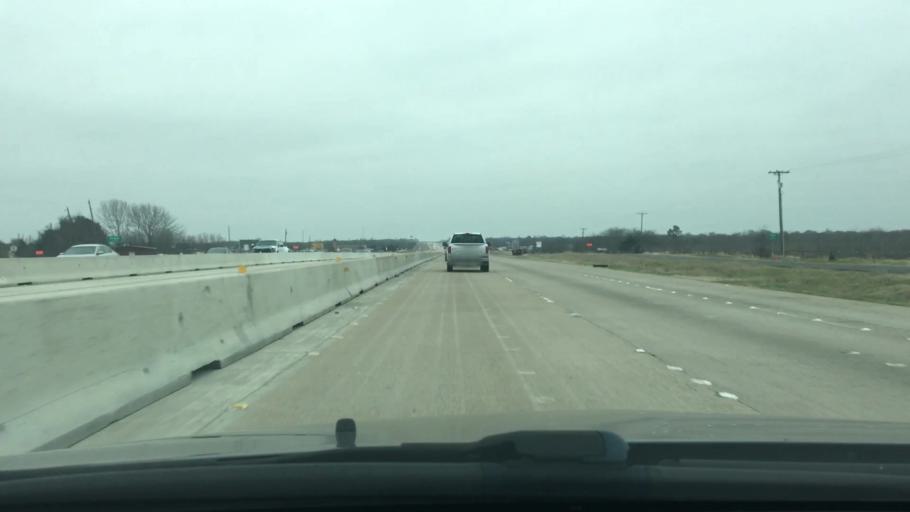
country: US
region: Texas
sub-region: Navarro County
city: Corsicana
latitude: 32.0312
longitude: -96.4432
